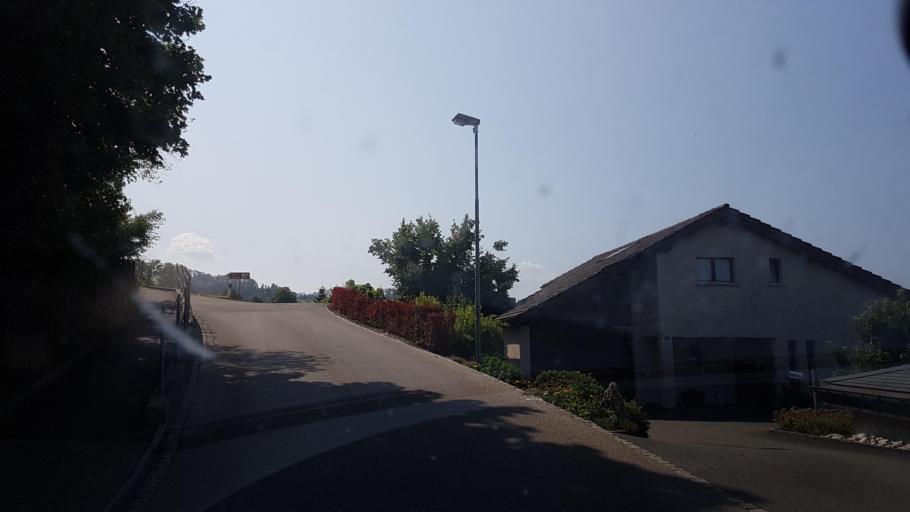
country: CH
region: Saint Gallen
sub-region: Wahlkreis Toggenburg
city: Mogelsberg
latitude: 47.3607
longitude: 9.1358
